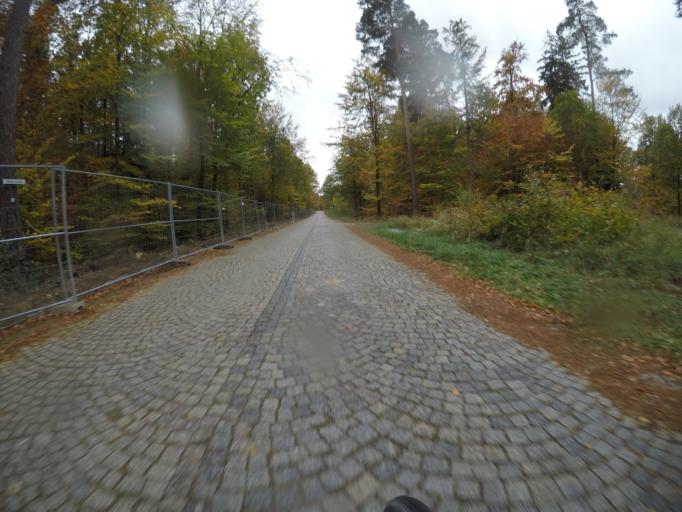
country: DE
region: Baden-Wuerttemberg
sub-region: Regierungsbezirk Stuttgart
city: Schonaich
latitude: 48.7050
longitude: 9.0737
